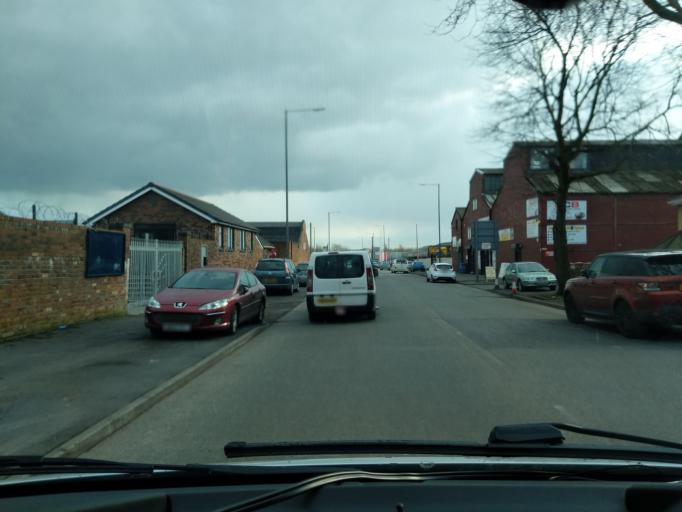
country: GB
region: England
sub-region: St. Helens
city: St Helens
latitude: 53.4523
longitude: -2.7231
